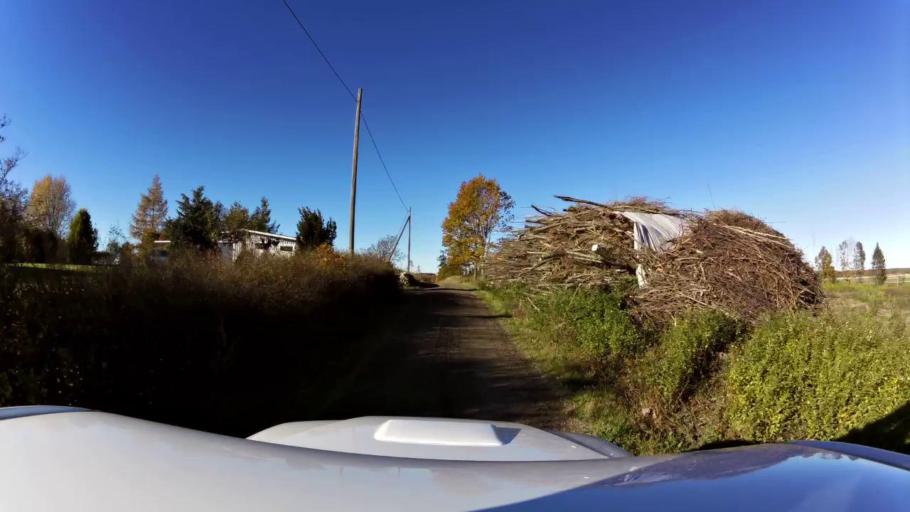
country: SE
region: OEstergoetland
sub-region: Linkopings Kommun
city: Ljungsbro
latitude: 58.5136
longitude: 15.4044
